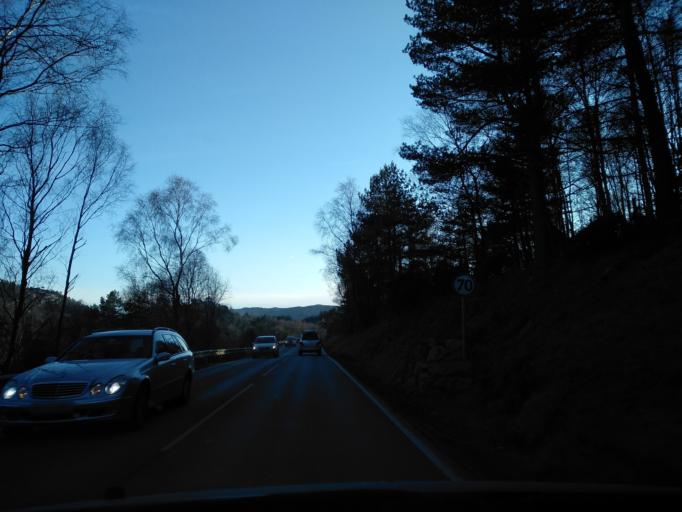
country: NO
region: Rogaland
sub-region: Tysvaer
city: Aksdal
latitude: 59.4612
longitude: 5.5101
